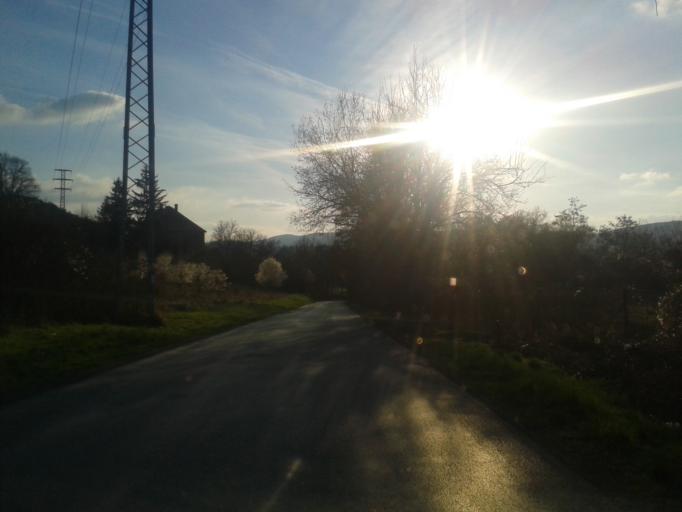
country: CZ
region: Central Bohemia
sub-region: Okres Beroun
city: Kraluv Dvur
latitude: 49.9377
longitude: 14.0396
